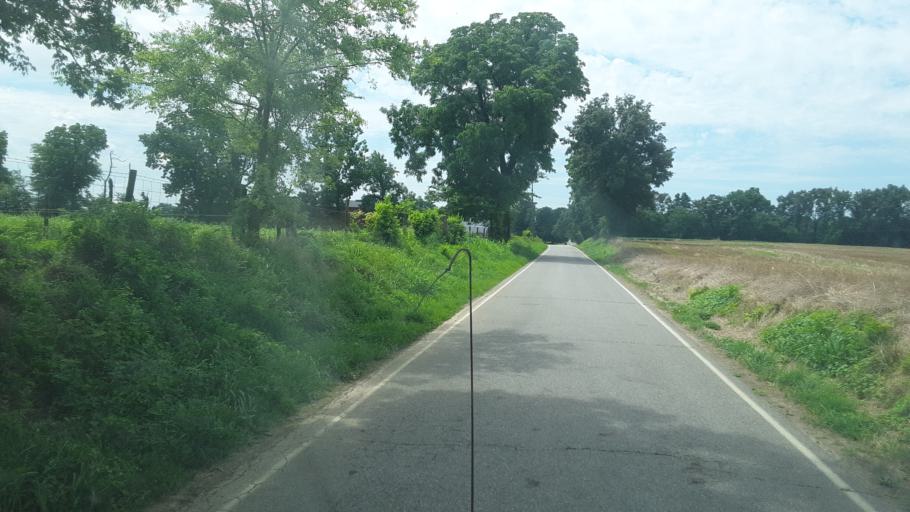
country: US
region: Kentucky
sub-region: Christian County
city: Oak Grove
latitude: 36.6521
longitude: -87.3441
